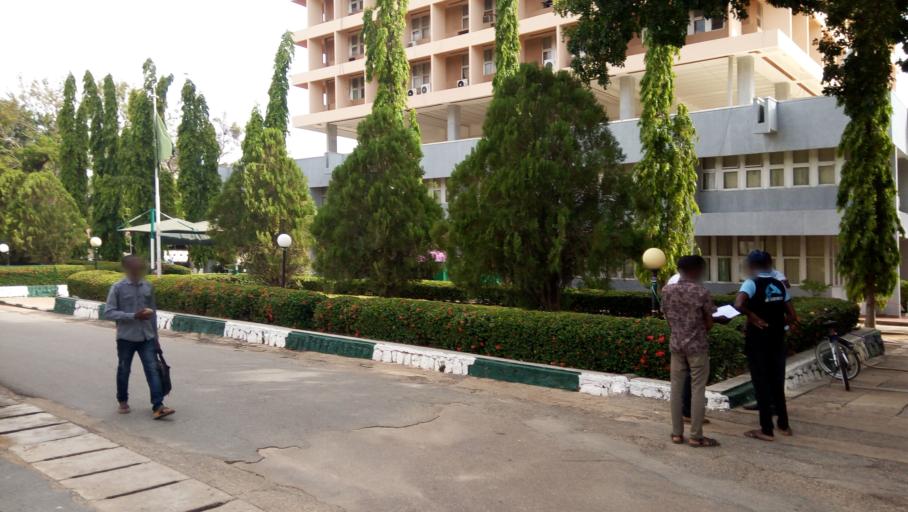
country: NG
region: Kaduna
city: Zaria
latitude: 11.1511
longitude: 7.6549
